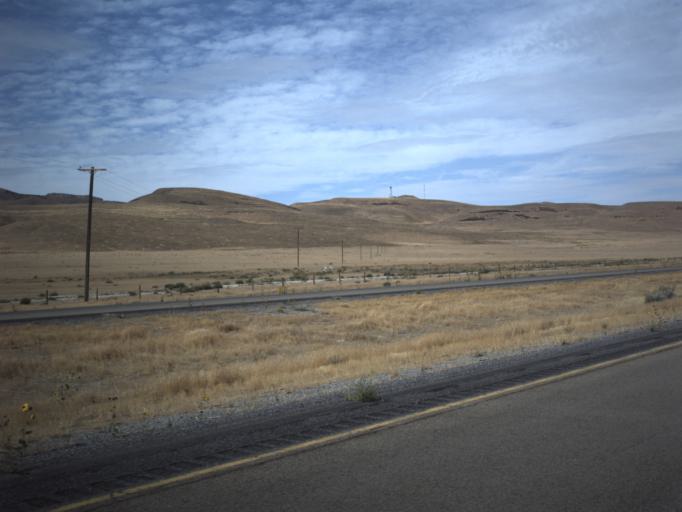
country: US
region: Utah
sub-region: Tooele County
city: Grantsville
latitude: 40.7988
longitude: -112.8467
